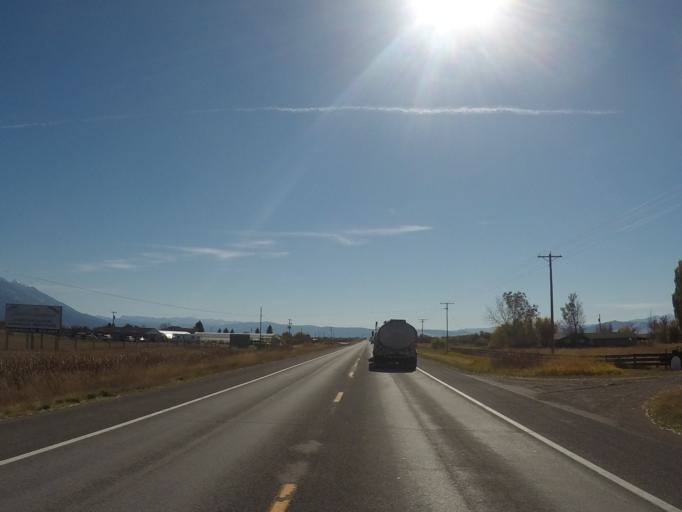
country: US
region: Montana
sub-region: Lake County
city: Ronan
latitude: 47.4897
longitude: -114.0969
